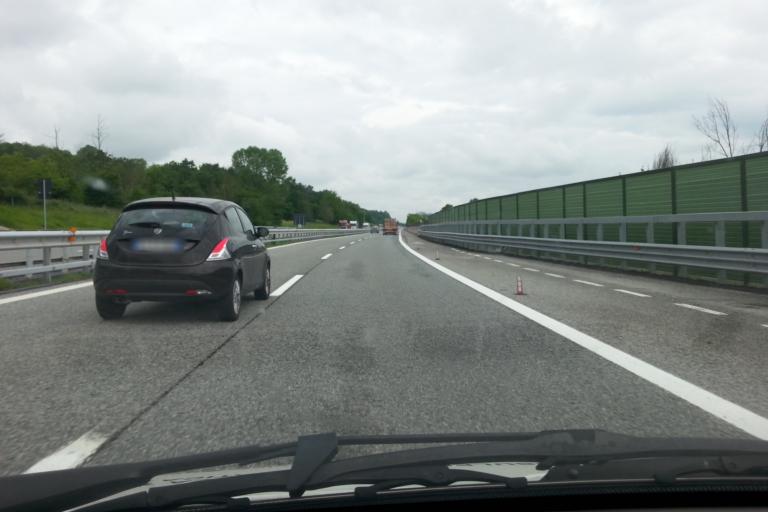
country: IT
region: Piedmont
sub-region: Provincia di Cuneo
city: Niella Tanaro
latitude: 44.4048
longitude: 7.9225
